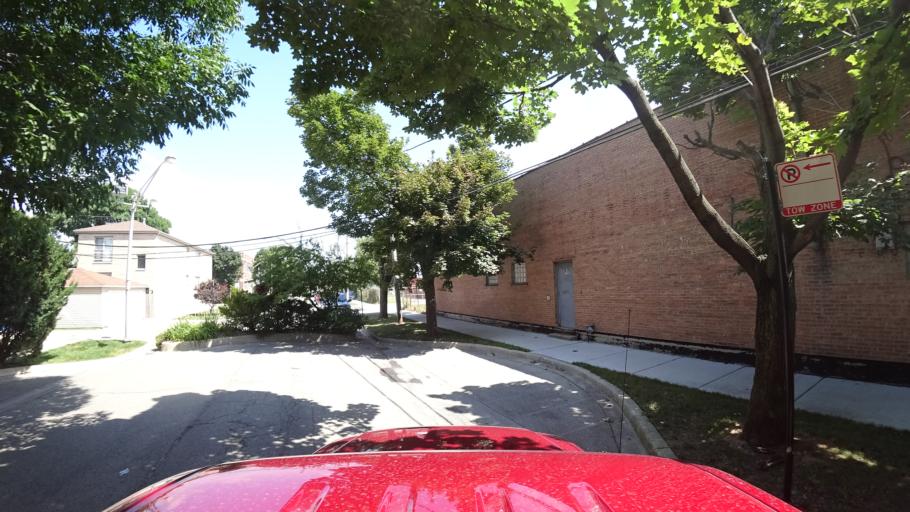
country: US
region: Illinois
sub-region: Cook County
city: Chicago
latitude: 41.8284
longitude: -87.6388
